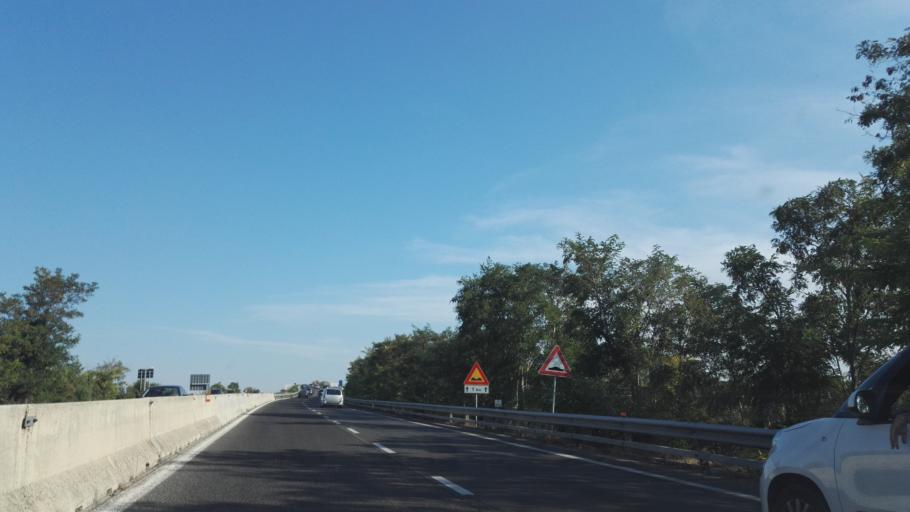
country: IT
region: Apulia
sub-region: Provincia di Bari
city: Polignano a Mare
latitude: 41.0016
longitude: 17.1993
